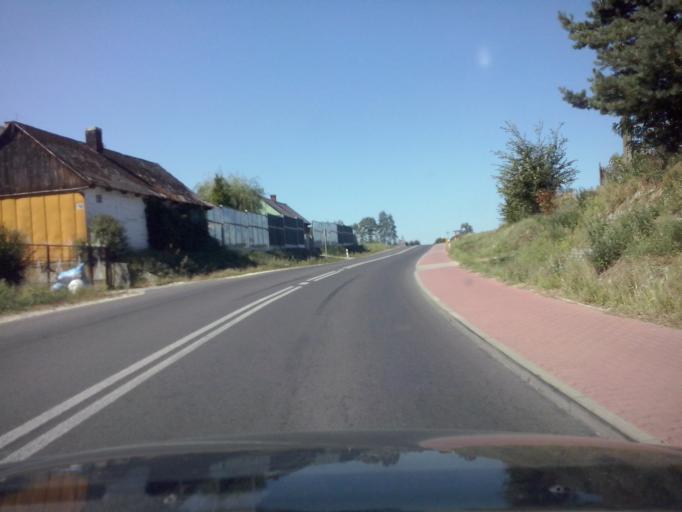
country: PL
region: Swietokrzyskie
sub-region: Powiat buski
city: Gnojno
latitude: 50.5854
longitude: 20.9238
